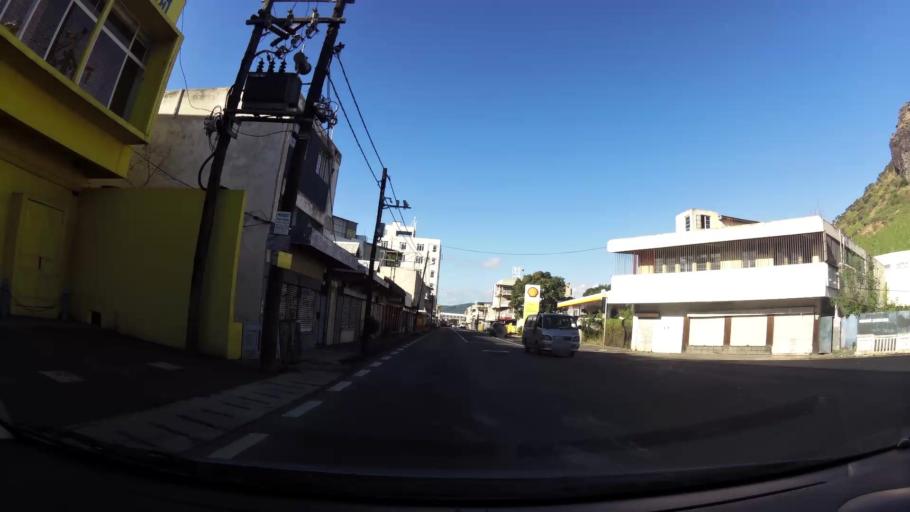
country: MU
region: Port Louis
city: Port Louis
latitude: -20.1675
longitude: 57.4865
